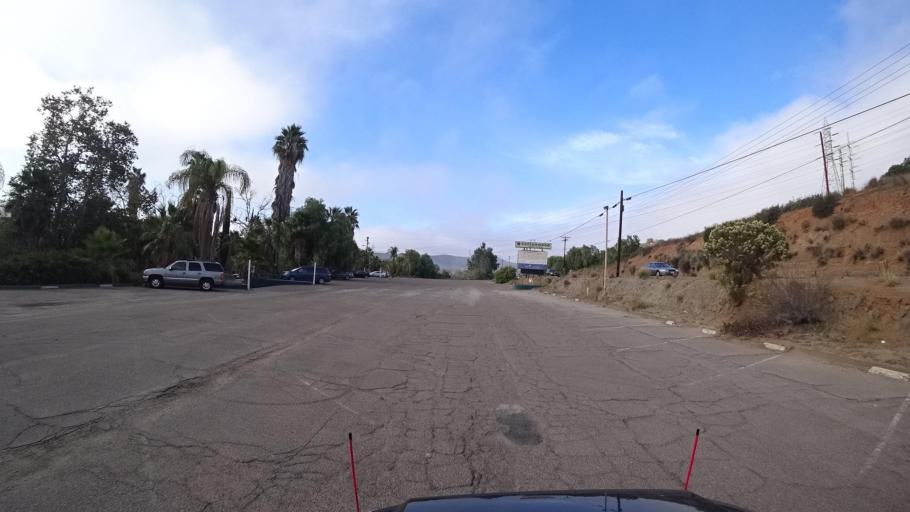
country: US
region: California
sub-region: San Diego County
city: Rancho San Diego
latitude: 32.7491
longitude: -116.9104
